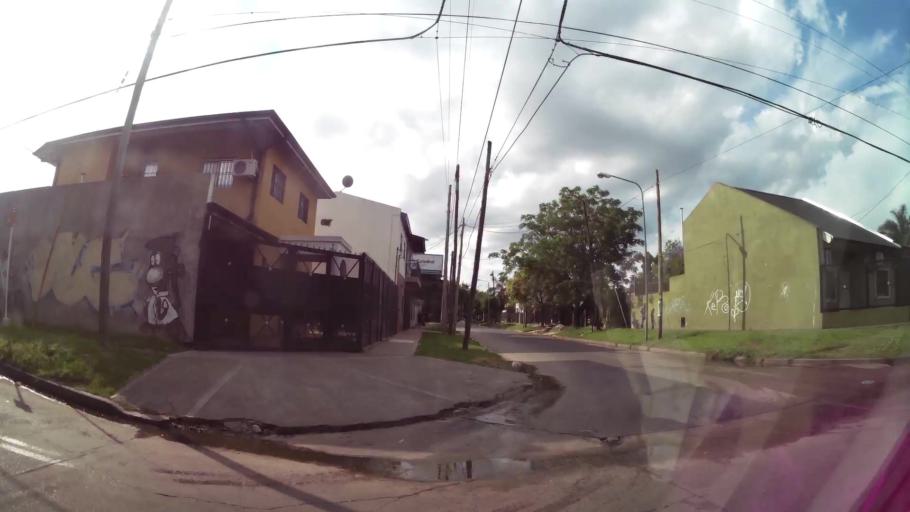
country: AR
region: Buenos Aires
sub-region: Partido de Tigre
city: Tigre
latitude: -34.4698
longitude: -58.6576
